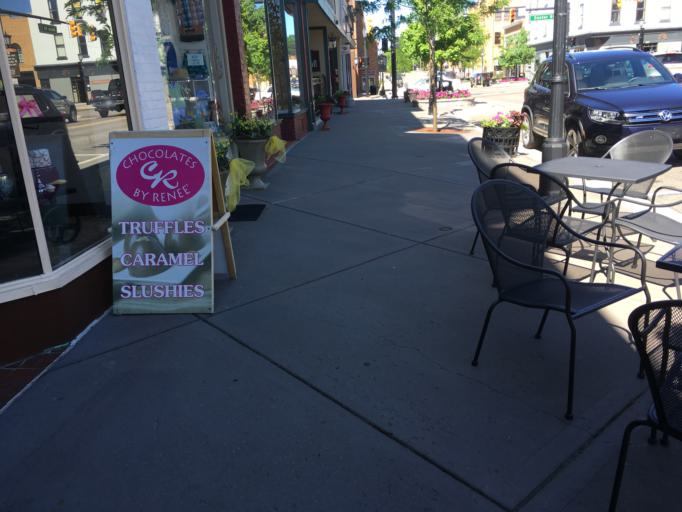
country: US
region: Michigan
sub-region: Wayne County
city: Northville
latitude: 42.4311
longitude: -83.4826
